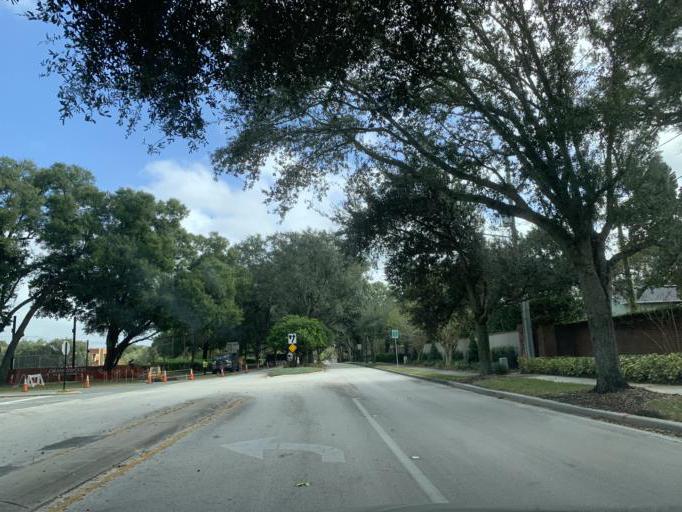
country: US
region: Florida
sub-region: Orange County
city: Eatonville
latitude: 28.6292
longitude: -81.3833
